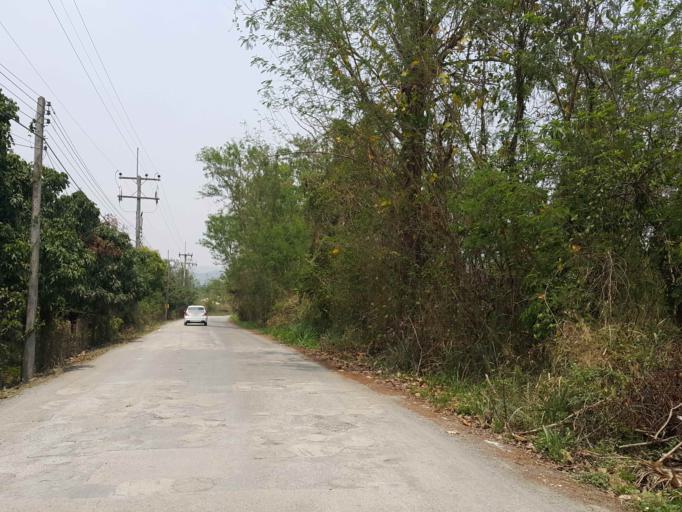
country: TH
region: Chiang Mai
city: San Sai
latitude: 18.9164
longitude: 99.0303
